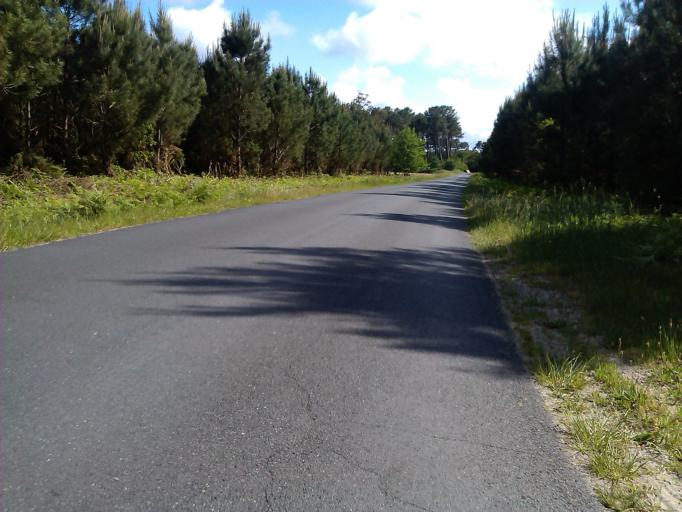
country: FR
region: Aquitaine
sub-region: Departement des Landes
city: Leon
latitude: 43.8614
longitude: -1.3571
